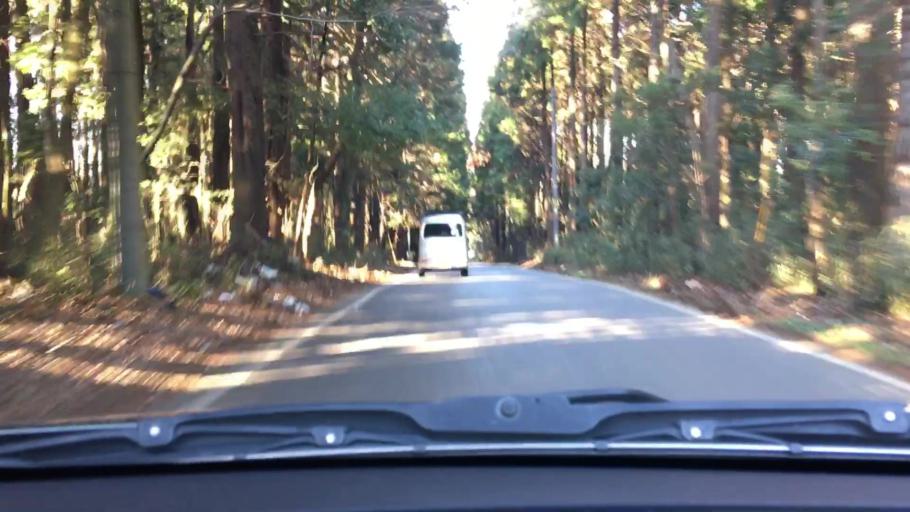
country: JP
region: Chiba
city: Shisui
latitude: 35.7009
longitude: 140.2881
